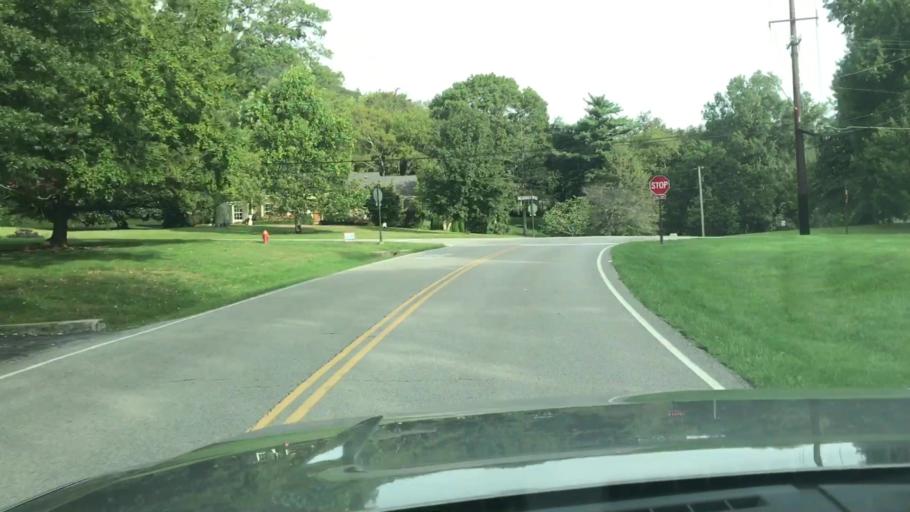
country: US
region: Tennessee
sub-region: Davidson County
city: Forest Hills
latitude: 36.0660
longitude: -86.8278
